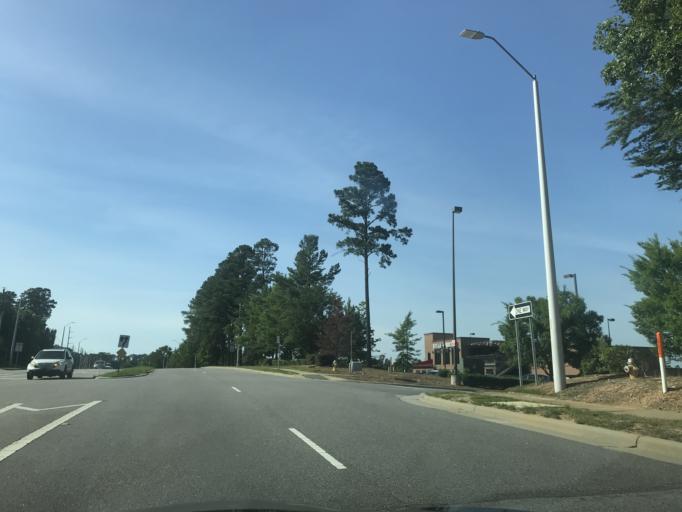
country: US
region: North Carolina
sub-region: Wake County
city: Garner
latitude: 35.6870
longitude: -78.5808
